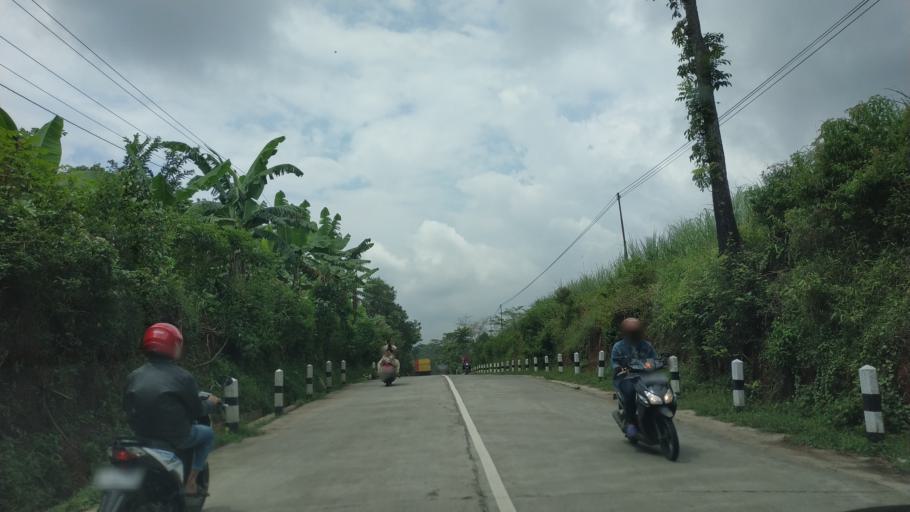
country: ID
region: Central Java
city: Weleri
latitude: -7.1020
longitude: 110.0675
